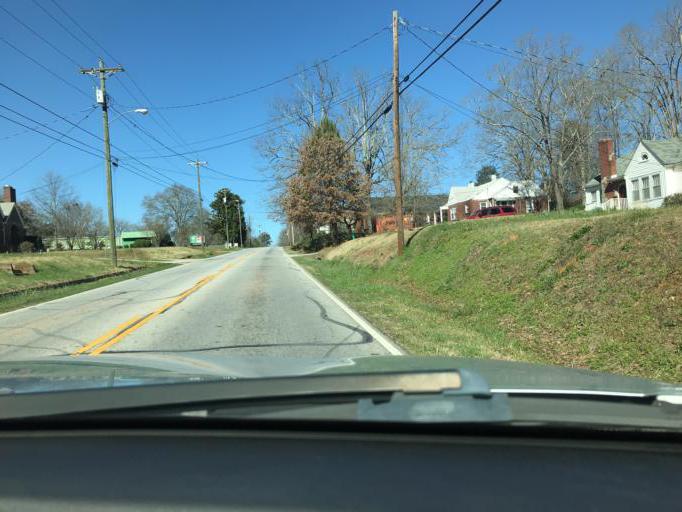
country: US
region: South Carolina
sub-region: Laurens County
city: Watts Mills
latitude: 34.4968
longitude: -81.9930
